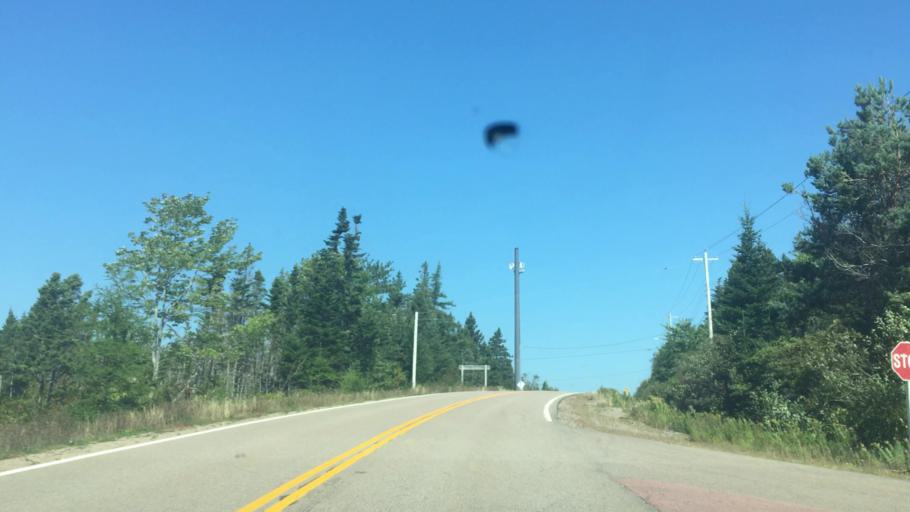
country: CA
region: Nova Scotia
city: Antigonish
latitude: 45.0242
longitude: -62.0315
